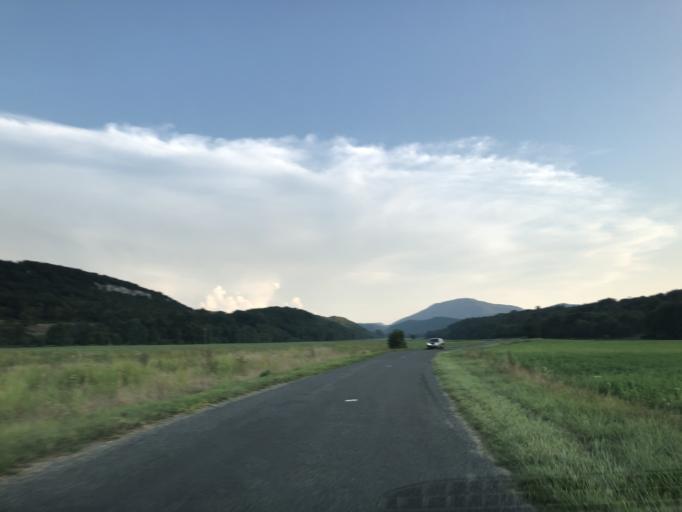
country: FR
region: Rhone-Alpes
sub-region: Departement de l'Ain
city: Belley
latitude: 45.7624
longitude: 5.6228
